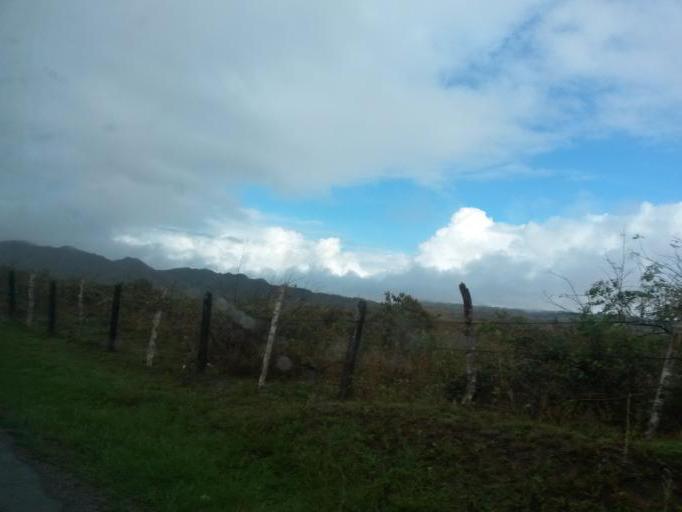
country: CO
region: Cauca
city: El Bordo
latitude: 2.1478
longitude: -76.9247
